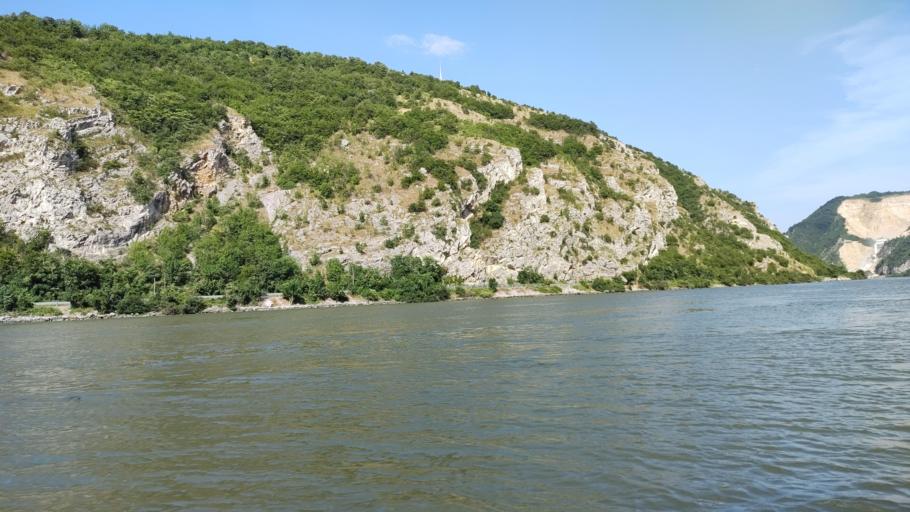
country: RO
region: Caras-Severin
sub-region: Comuna Pescari
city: Coronini
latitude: 44.6578
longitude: 21.7082
